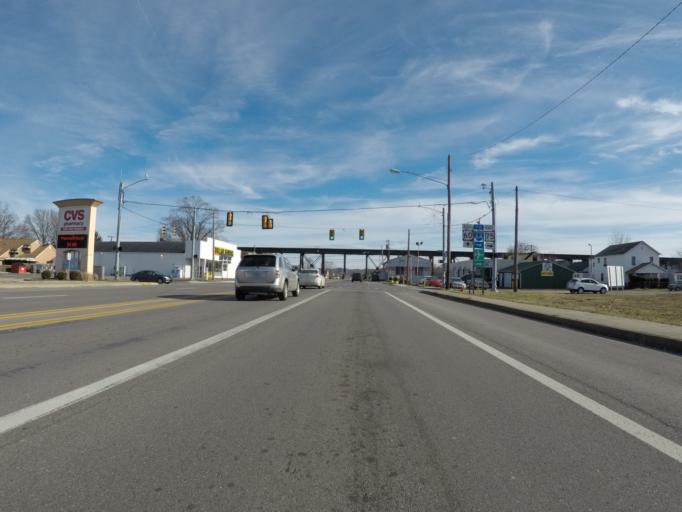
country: US
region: West Virginia
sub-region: Wayne County
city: Kenova
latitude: 38.4011
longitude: -82.5776
